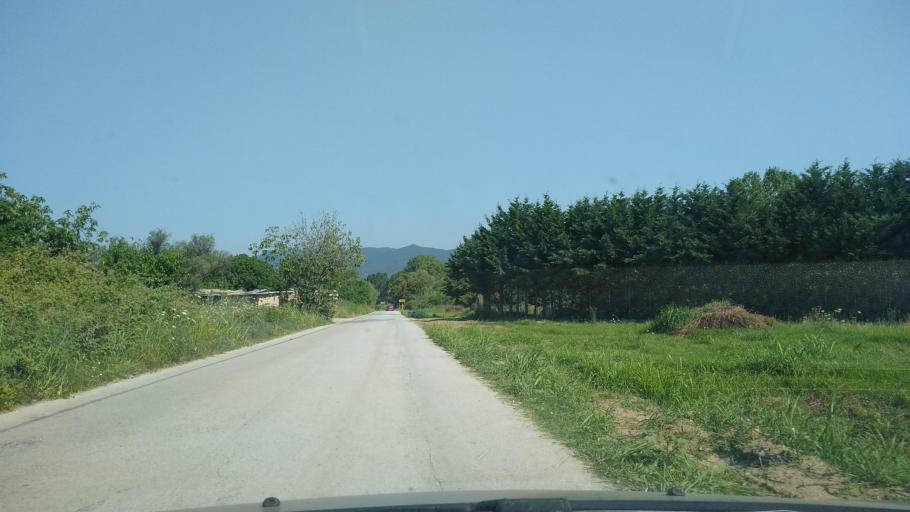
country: GR
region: Central Macedonia
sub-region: Nomos Thessalonikis
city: Stavros
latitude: 40.6737
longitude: 23.6900
